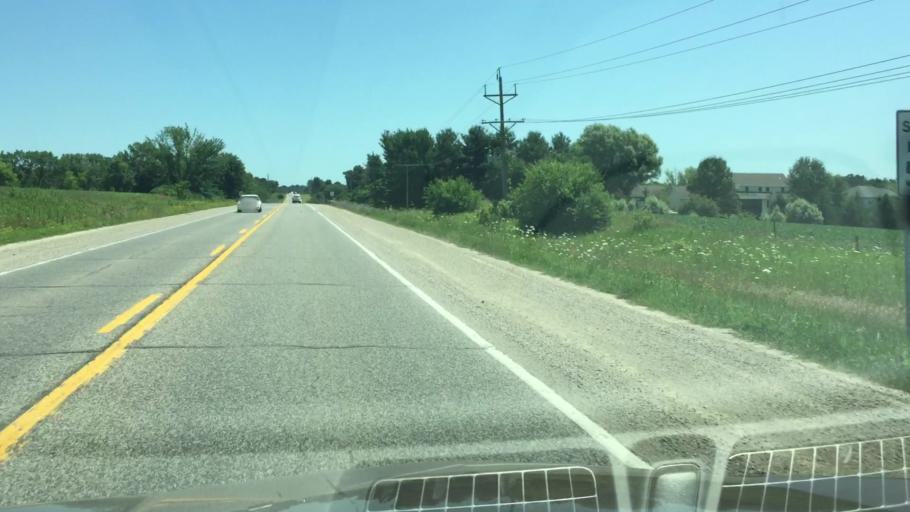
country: US
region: Iowa
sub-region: Linn County
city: Mount Vernon
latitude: 41.9161
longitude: -91.4178
